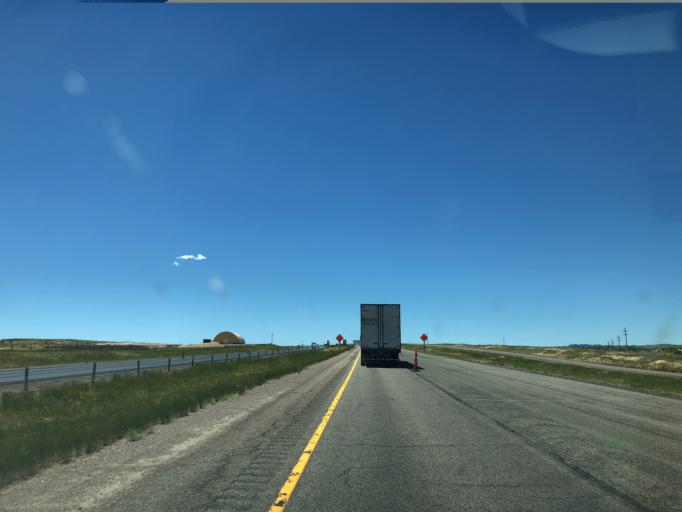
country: US
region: Wyoming
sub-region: Laramie County
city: Cheyenne
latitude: 41.0996
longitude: -105.1454
